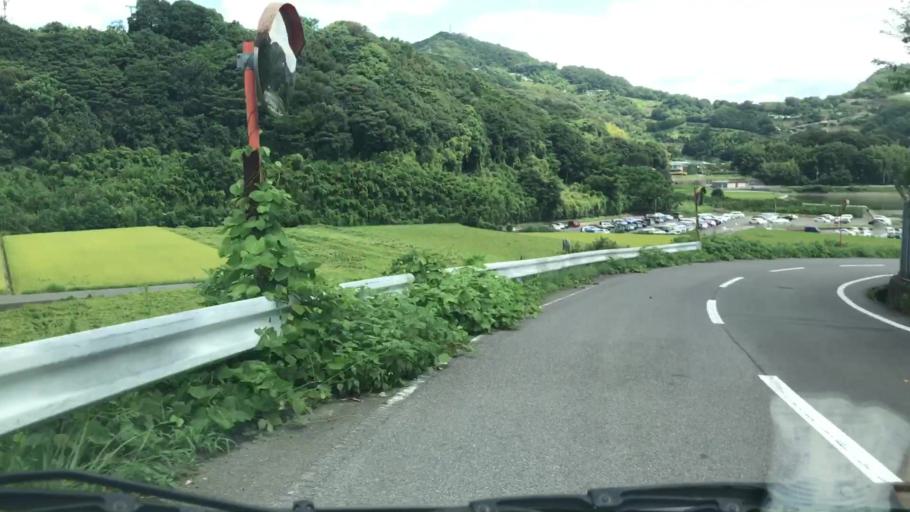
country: JP
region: Saga Prefecture
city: Takeocho-takeo
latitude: 33.2328
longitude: 130.1421
